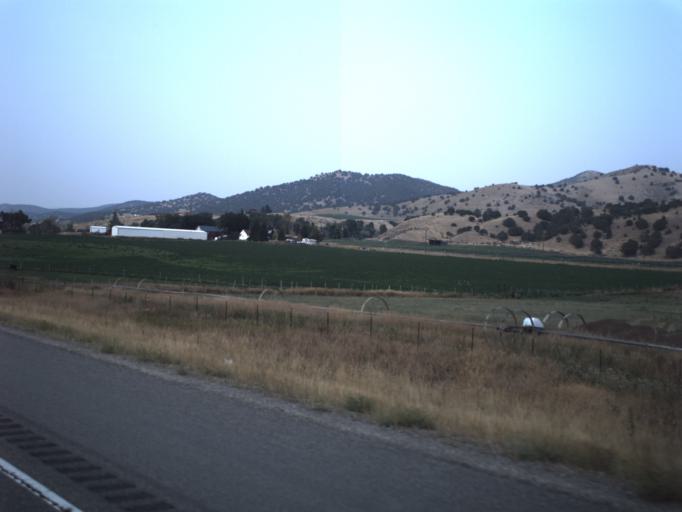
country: US
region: Utah
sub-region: Summit County
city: Coalville
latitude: 40.8426
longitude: -111.3871
